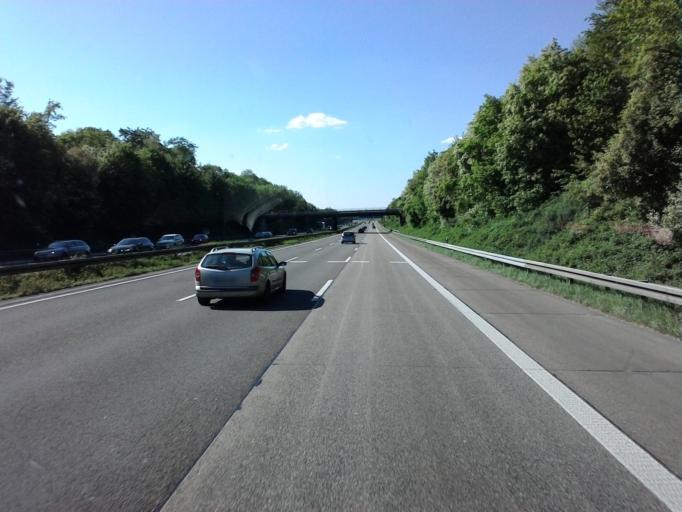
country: DE
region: North Rhine-Westphalia
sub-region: Regierungsbezirk Dusseldorf
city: Ratingen
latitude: 51.3385
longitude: 6.8743
